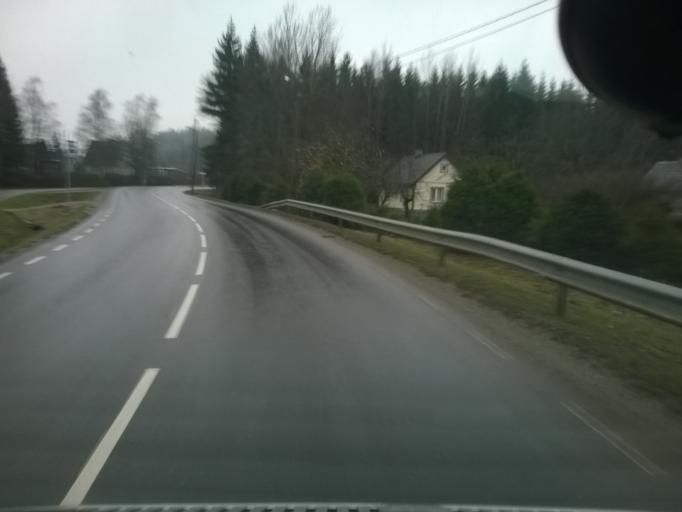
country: EE
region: Harju
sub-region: Saku vald
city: Saku
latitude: 59.2411
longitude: 24.6811
